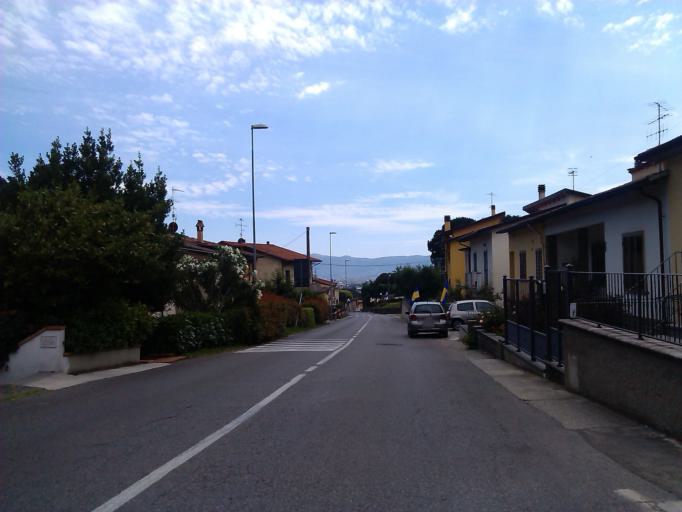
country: IT
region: Tuscany
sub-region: Provincia di Prato
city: Montemurlo
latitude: 43.9533
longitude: 11.0371
